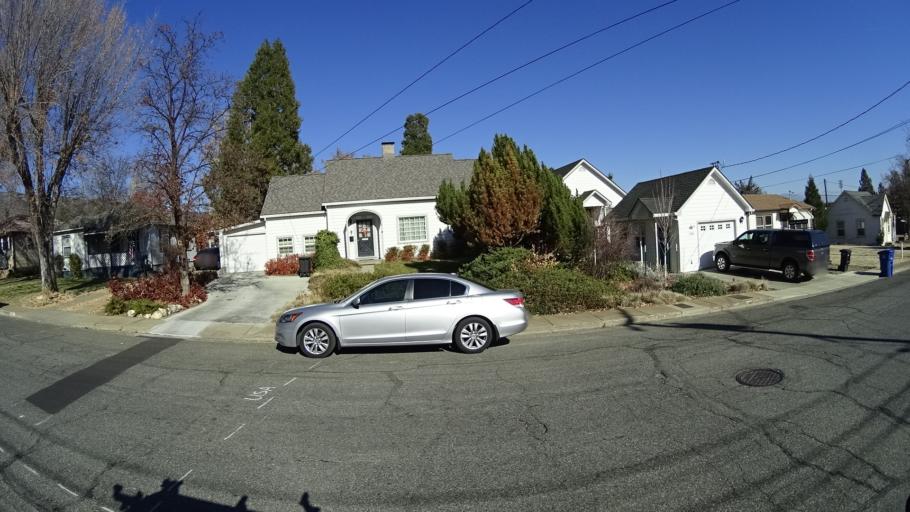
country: US
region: California
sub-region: Siskiyou County
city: Yreka
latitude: 41.7376
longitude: -122.6408
